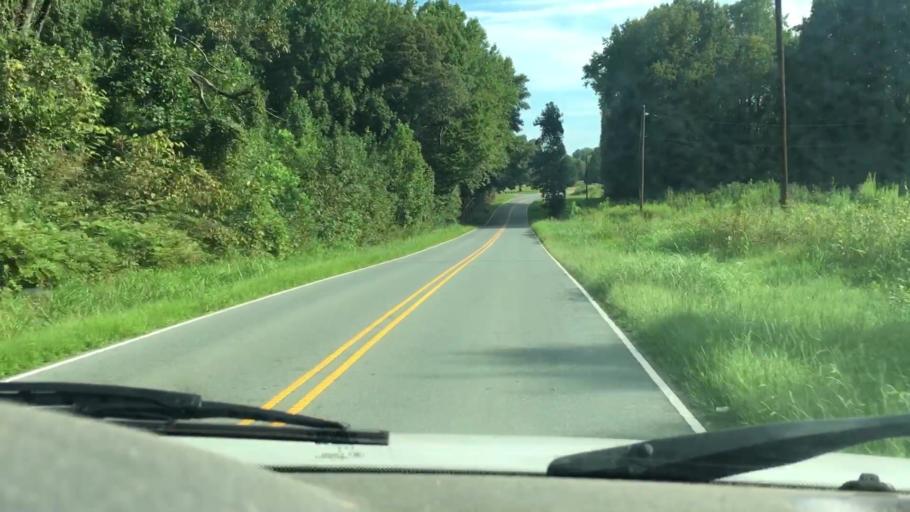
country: US
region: North Carolina
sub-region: Mecklenburg County
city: Huntersville
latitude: 35.3617
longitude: -80.8205
